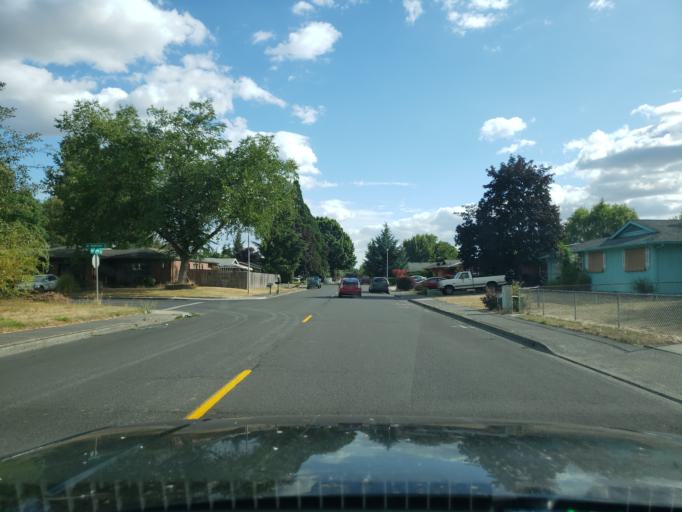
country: US
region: Oregon
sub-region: Yamhill County
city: McMinnville
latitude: 45.2076
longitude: -123.2196
